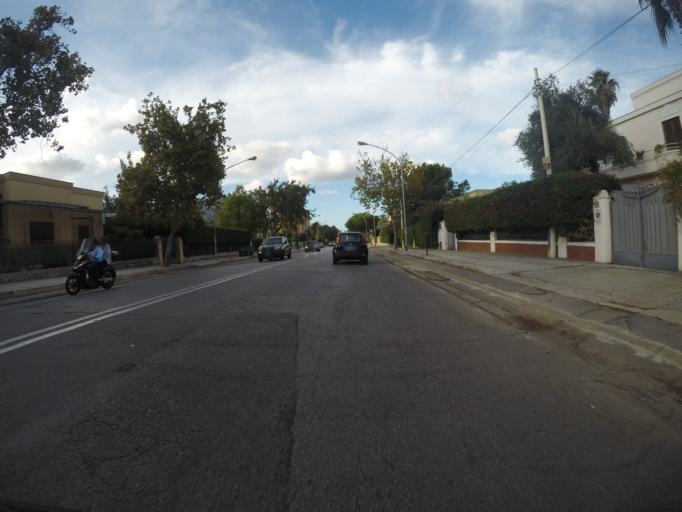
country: IT
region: Sicily
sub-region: Palermo
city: Palermo
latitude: 38.1921
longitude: 13.3325
